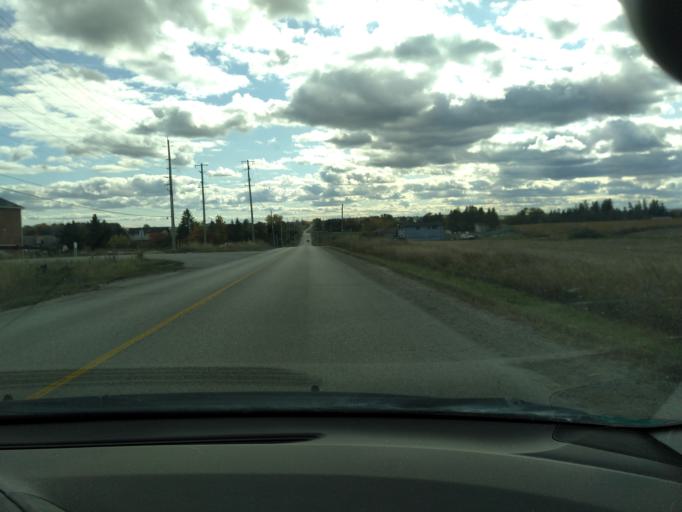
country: CA
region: Ontario
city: Bradford West Gwillimbury
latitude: 44.0991
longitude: -79.6000
